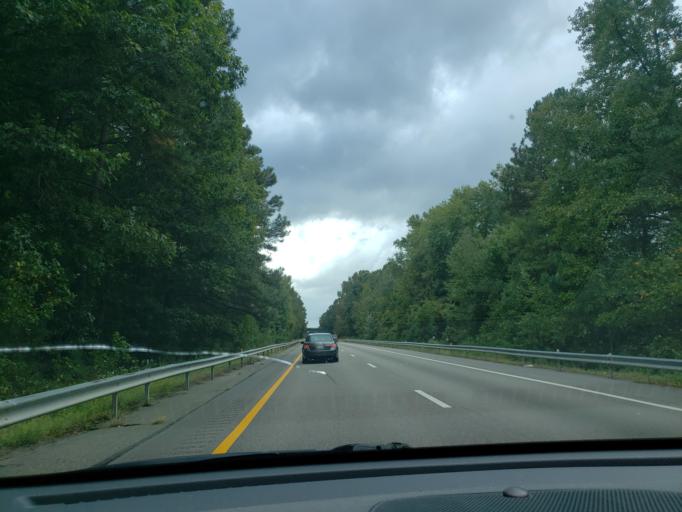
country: US
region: Virginia
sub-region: Mecklenburg County
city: South Hill
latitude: 36.6634
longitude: -78.1333
